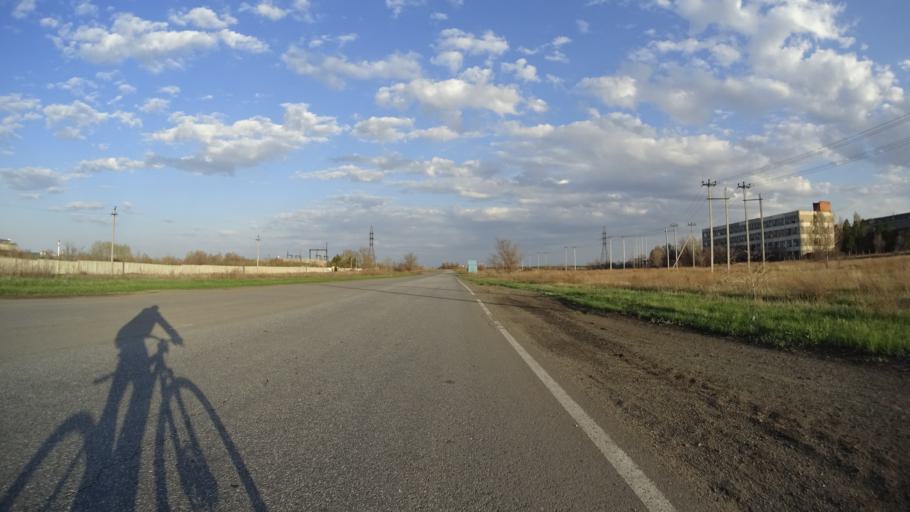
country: RU
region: Chelyabinsk
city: Troitsk
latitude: 54.0646
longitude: 61.5689
